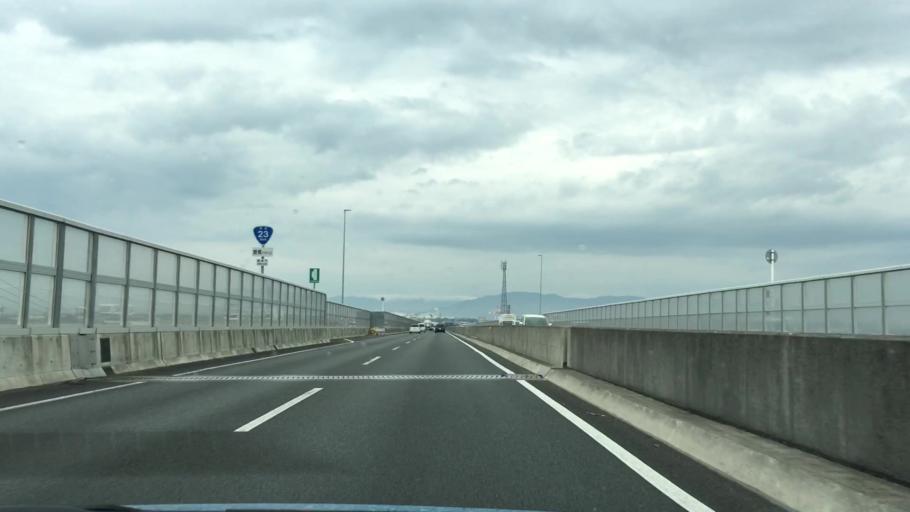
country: JP
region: Aichi
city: Toyohashi
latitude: 34.7401
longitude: 137.3423
